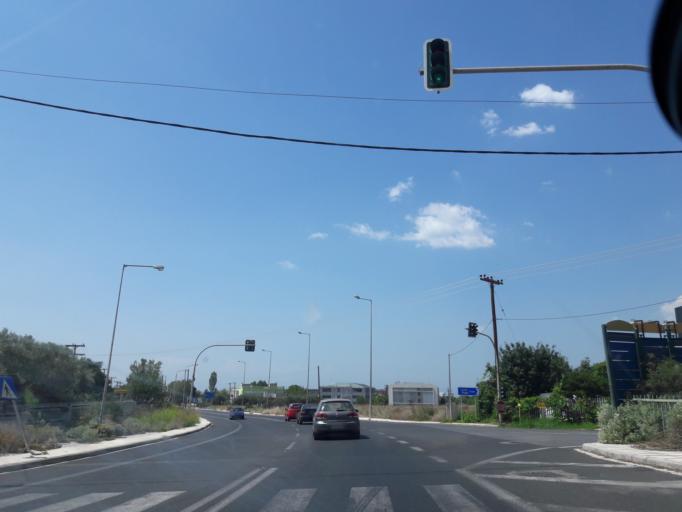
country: GR
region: Central Macedonia
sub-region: Nomos Thessalonikis
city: Thermi
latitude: 40.5409
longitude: 23.0231
